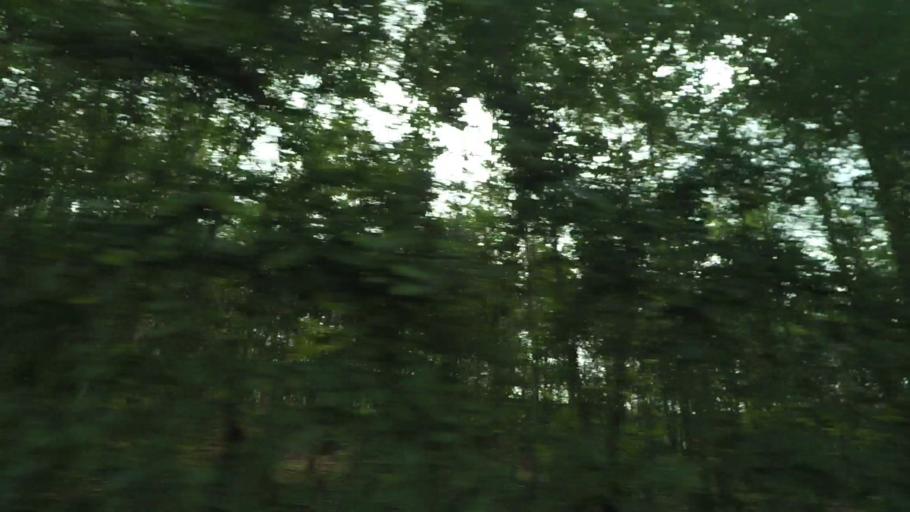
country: DK
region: Central Jutland
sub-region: Syddjurs Kommune
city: Ryomgard
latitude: 56.4401
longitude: 10.5599
